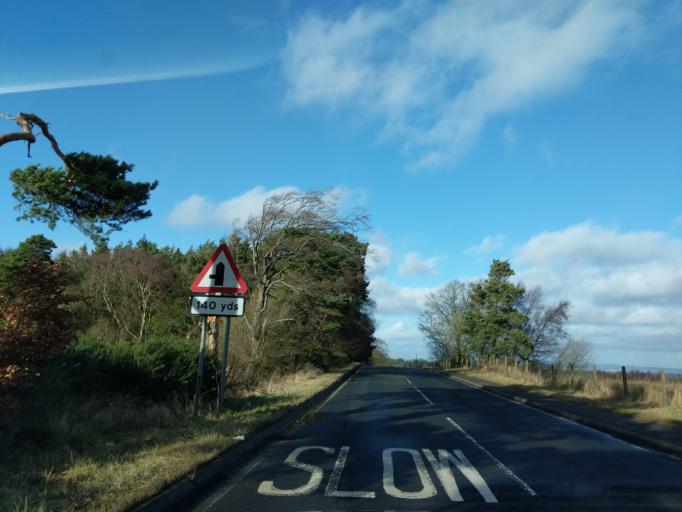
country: GB
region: Scotland
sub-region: West Lothian
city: Kirknewton
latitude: 55.8719
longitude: -3.4071
